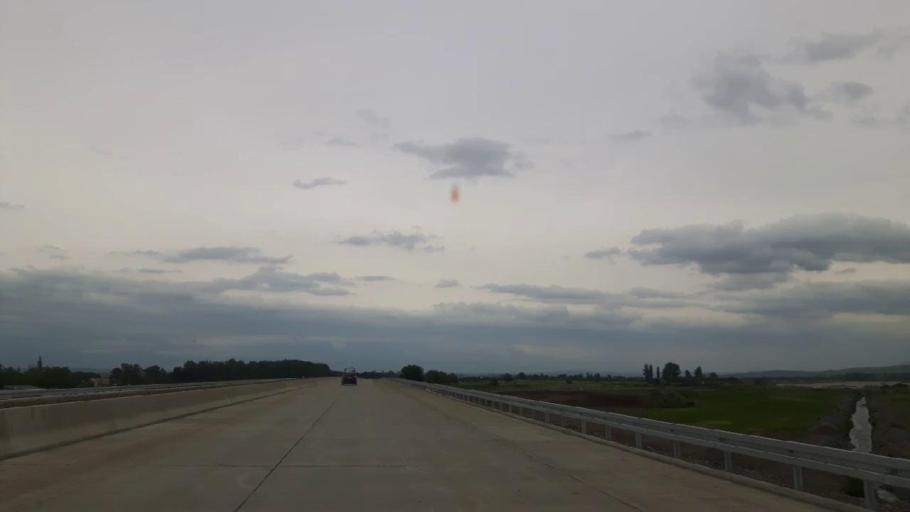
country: GE
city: Agara
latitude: 42.0231
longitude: 43.7539
